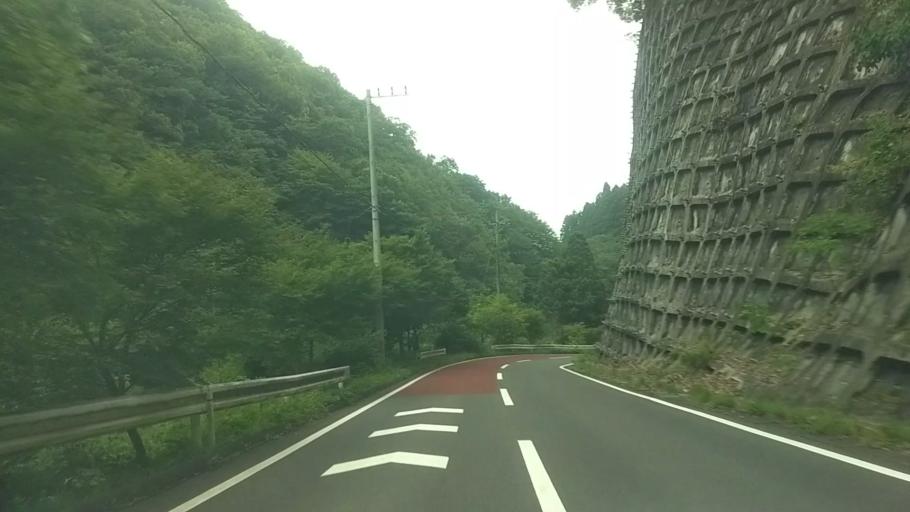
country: JP
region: Chiba
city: Kawaguchi
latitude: 35.2332
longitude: 140.0296
